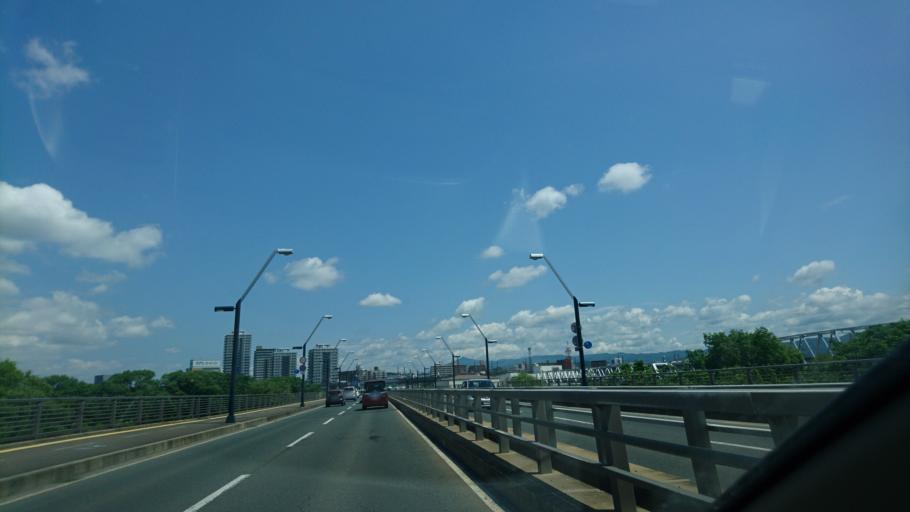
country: JP
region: Iwate
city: Morioka-shi
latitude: 39.6936
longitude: 141.1376
